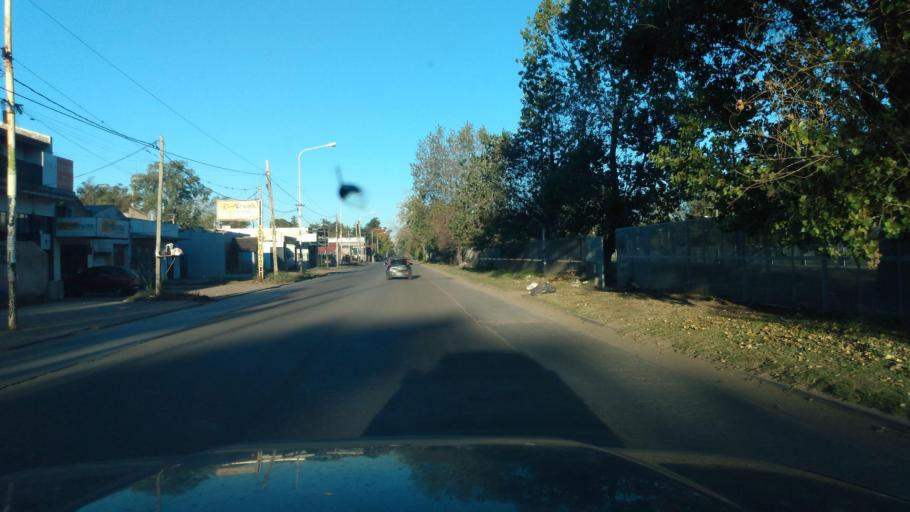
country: AR
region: Buenos Aires
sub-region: Partido de Merlo
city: Merlo
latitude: -34.6398
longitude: -58.8273
